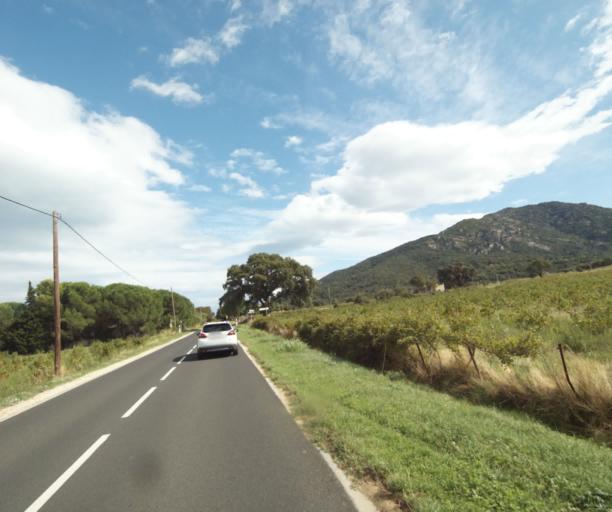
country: FR
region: Languedoc-Roussillon
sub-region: Departement des Pyrenees-Orientales
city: Sant Andreu de Sureda
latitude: 42.5317
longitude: 2.9816
